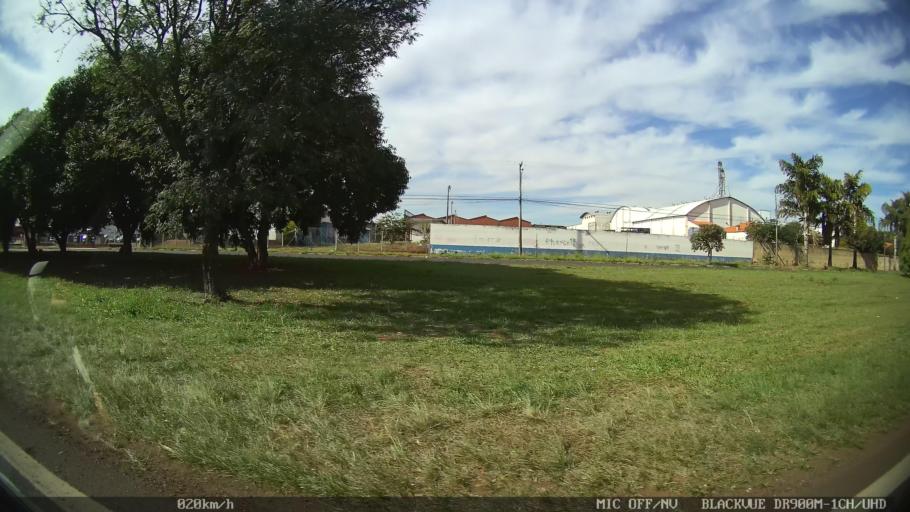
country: BR
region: Sao Paulo
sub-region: Araraquara
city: Araraquara
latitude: -21.8290
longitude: -48.1539
